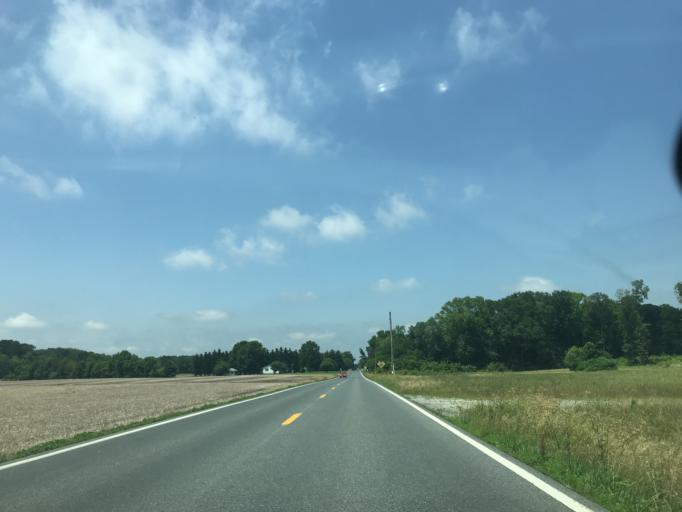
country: US
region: Maryland
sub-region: Dorchester County
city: Hurlock
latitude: 38.5965
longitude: -75.9523
